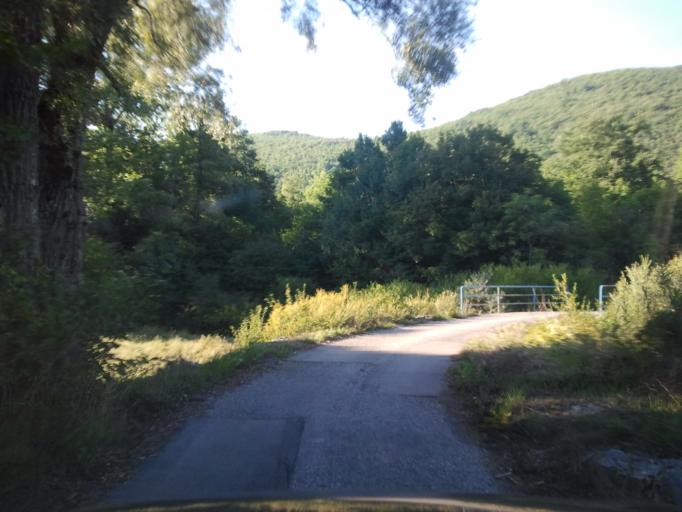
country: HR
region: Zadarska
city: Gracac
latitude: 44.3598
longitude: 15.7172
